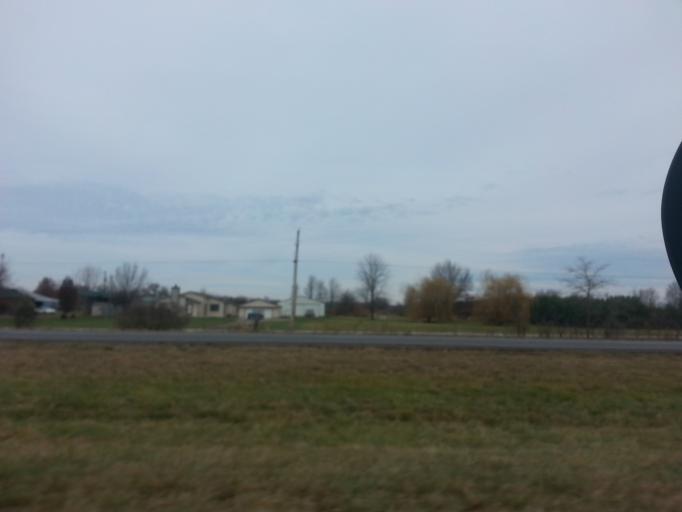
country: US
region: Indiana
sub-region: Hendricks County
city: Pittsboro
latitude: 39.8793
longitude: -86.4942
